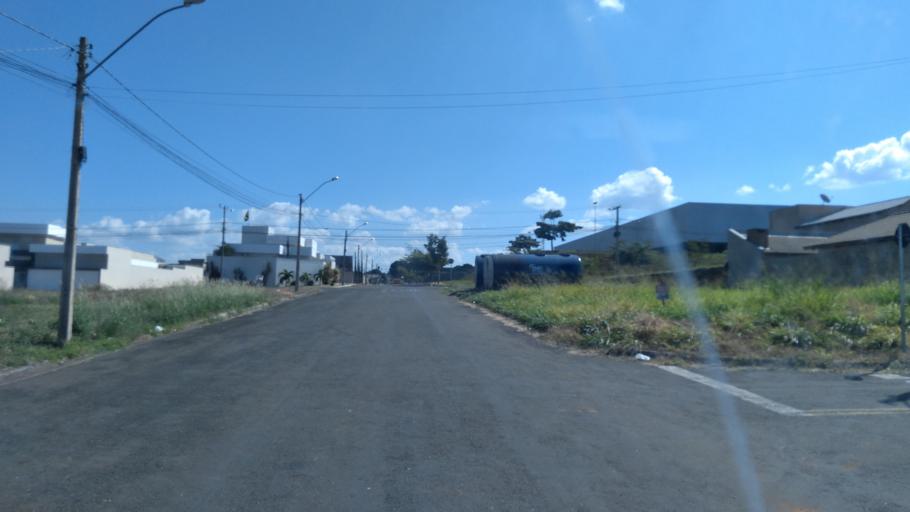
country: BR
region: Goias
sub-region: Mineiros
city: Mineiros
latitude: -17.5514
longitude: -52.5432
